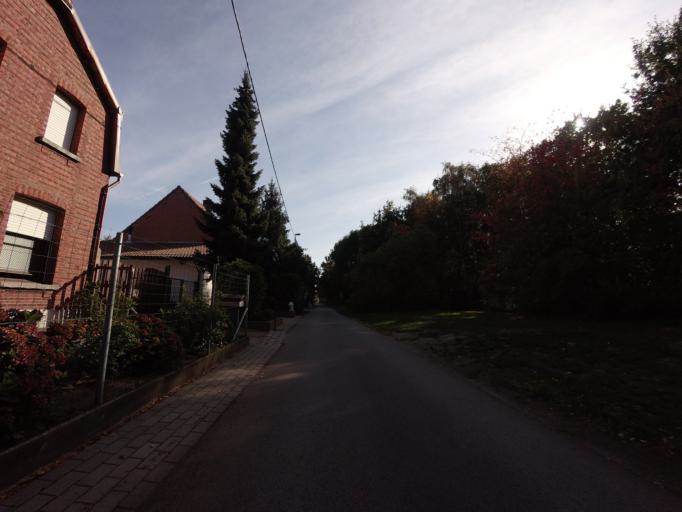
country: BE
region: Flanders
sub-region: Provincie Antwerpen
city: Stabroek
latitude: 51.3513
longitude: 4.3325
